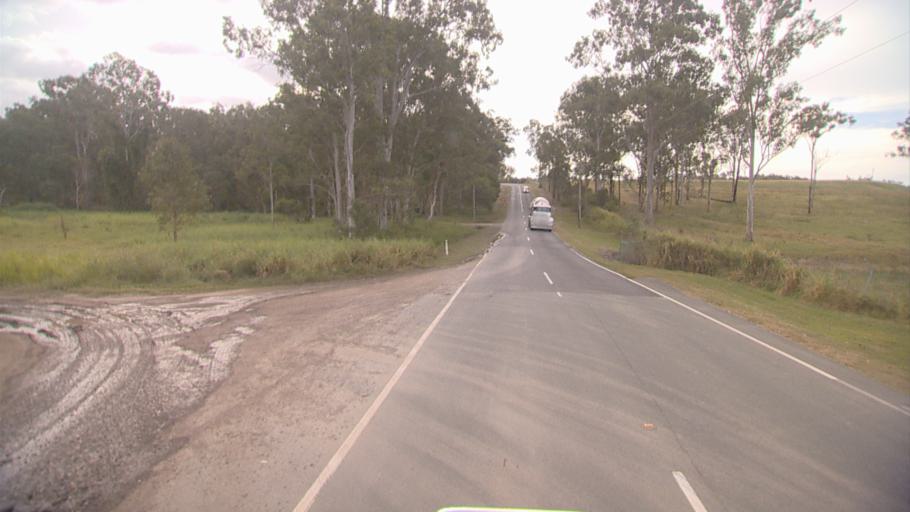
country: AU
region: Queensland
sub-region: Logan
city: Beenleigh
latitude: -27.7182
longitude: 153.1738
